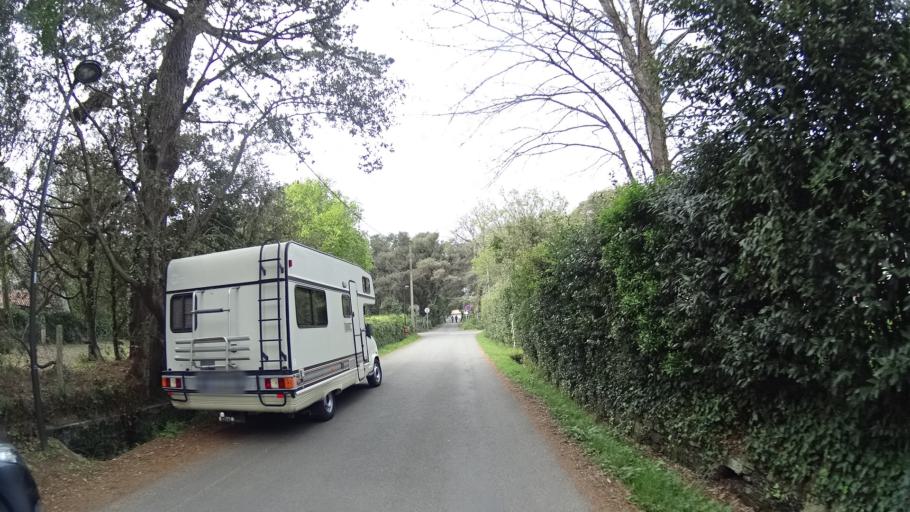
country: FR
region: Pays de la Loire
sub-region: Departement de la Vendee
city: La Gueriniere
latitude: 47.0117
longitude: -2.2273
